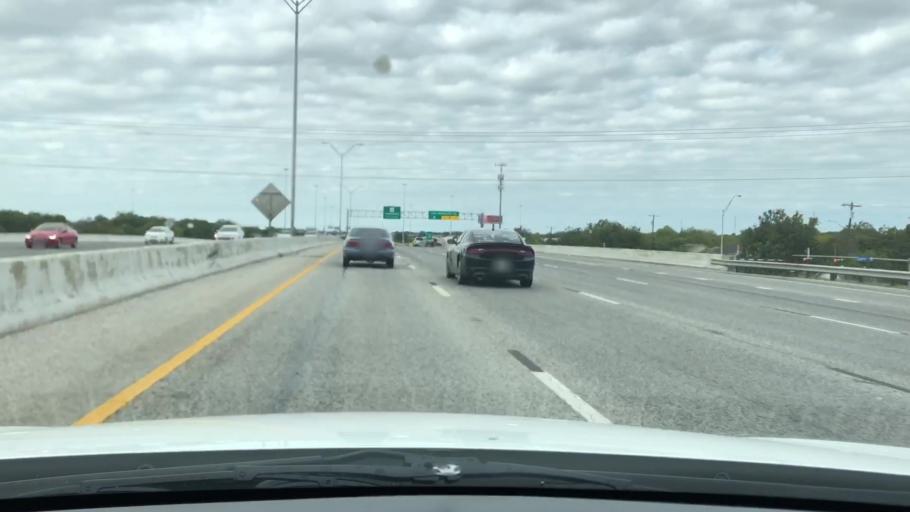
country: US
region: Texas
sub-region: Bexar County
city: San Antonio
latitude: 29.4040
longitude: -98.5477
